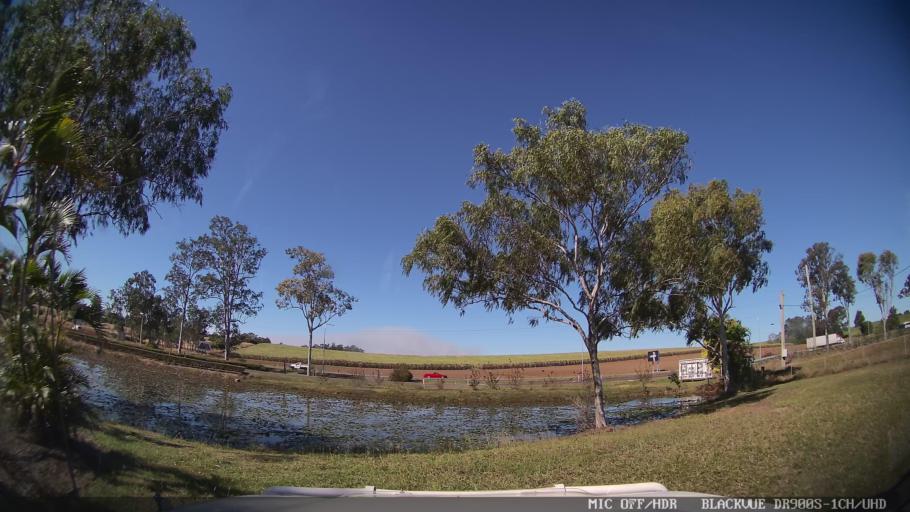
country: AU
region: Queensland
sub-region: Fraser Coast
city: Maryborough
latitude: -25.5779
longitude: 152.6539
